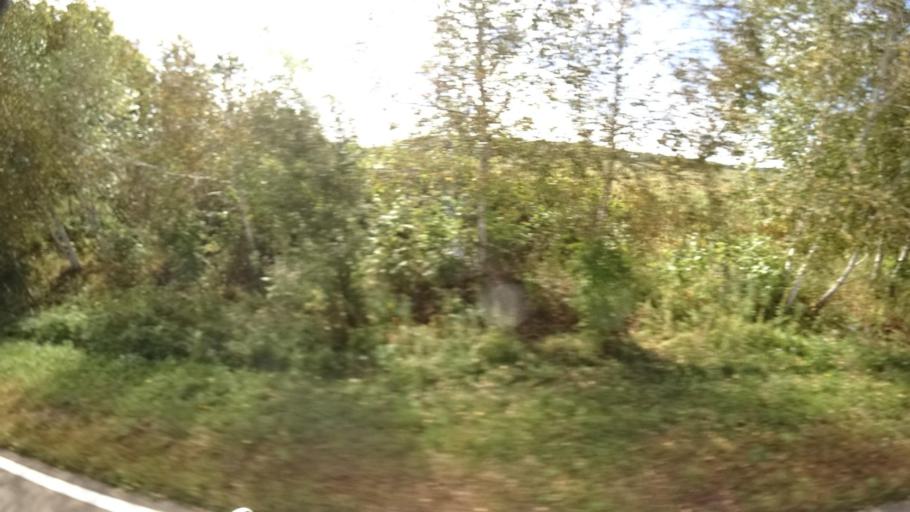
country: RU
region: Primorskiy
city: Yakovlevka
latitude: 44.4107
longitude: 133.5883
